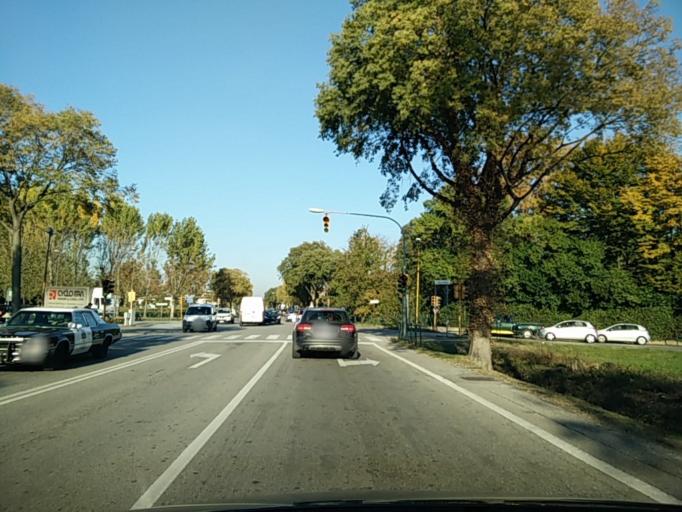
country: IT
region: Veneto
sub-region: Provincia di Treviso
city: Treviso
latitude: 45.6816
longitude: 12.2420
